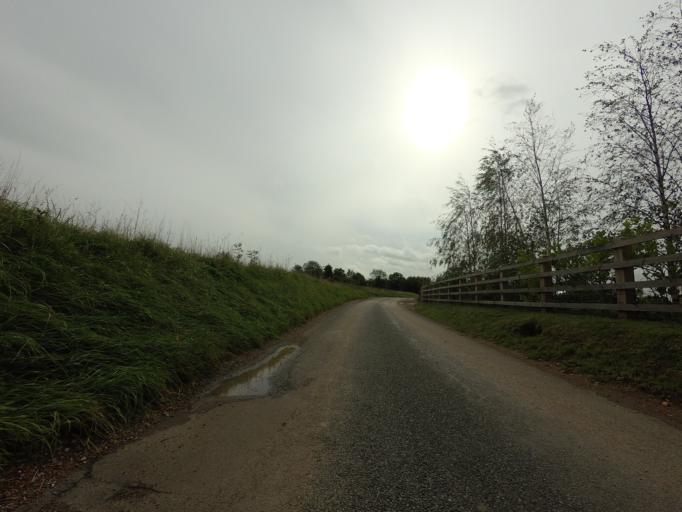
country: GB
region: England
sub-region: Hertfordshire
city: Reed
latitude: 51.9812
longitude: 0.0439
